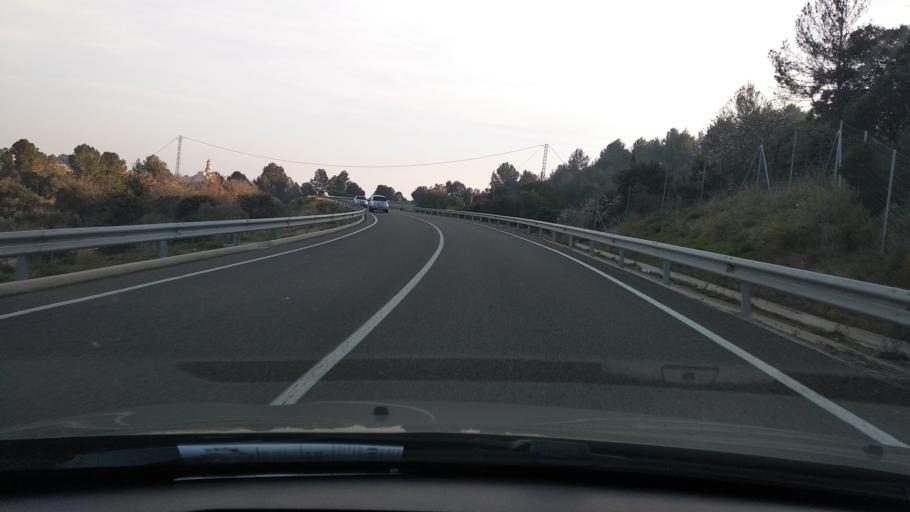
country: ES
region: Catalonia
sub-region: Provincia de Tarragona
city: les Borges del Camp
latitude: 41.1797
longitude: 1.0089
